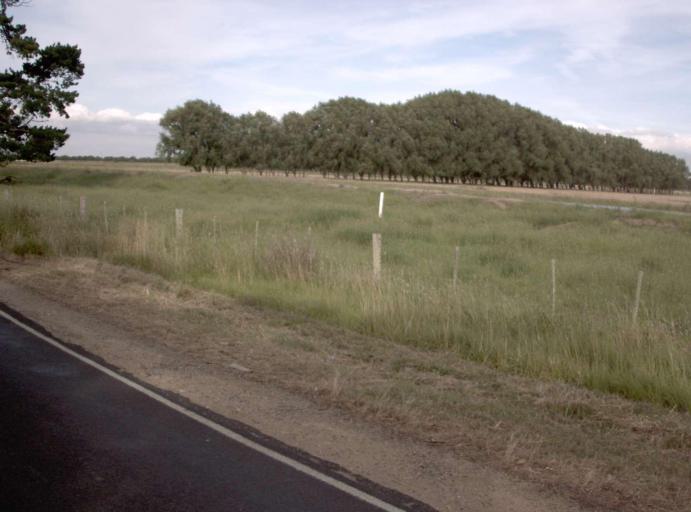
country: AU
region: Victoria
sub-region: Wellington
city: Heyfield
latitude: -38.0121
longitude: 146.7761
